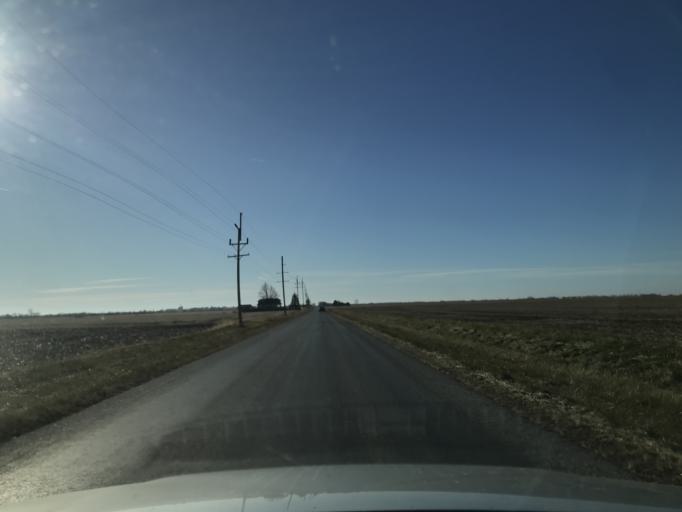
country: US
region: Illinois
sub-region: Hancock County
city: Carthage
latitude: 40.5026
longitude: -91.1781
